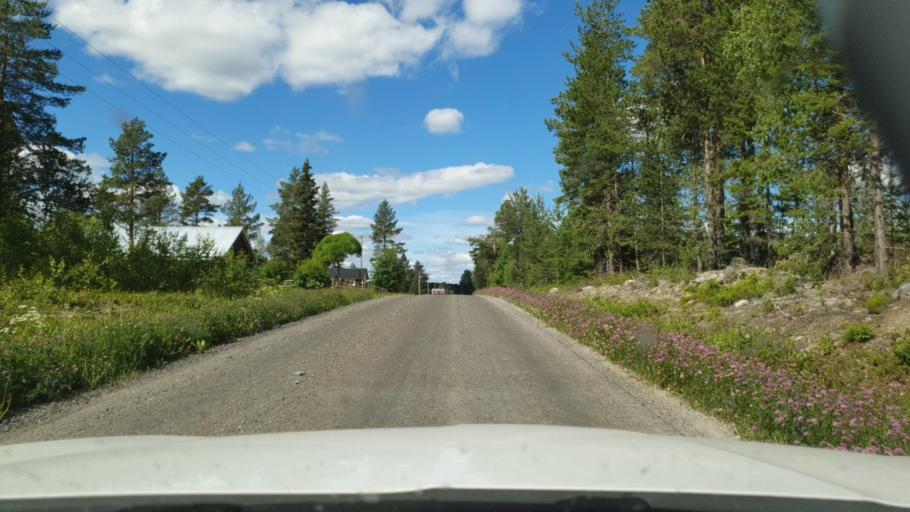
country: SE
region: Vaesterbotten
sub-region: Skelleftea Kommun
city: Backa
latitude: 65.1806
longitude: 21.0743
